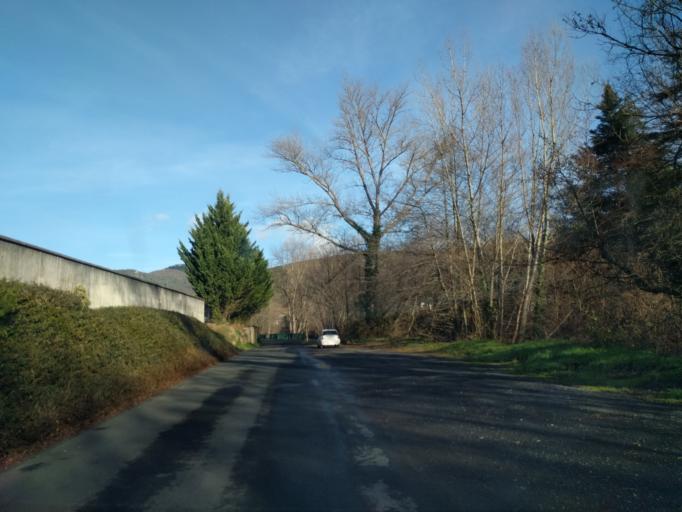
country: FR
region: Languedoc-Roussillon
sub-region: Departement de l'Aude
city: Quillan
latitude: 42.8799
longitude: 2.1869
